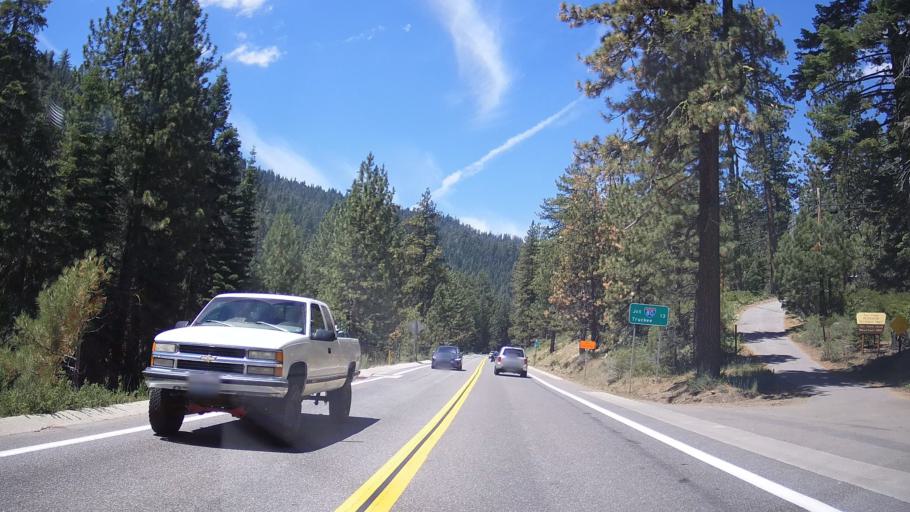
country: US
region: California
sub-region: Placer County
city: Sunnyside-Tahoe City
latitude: 39.1639
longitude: -120.1564
